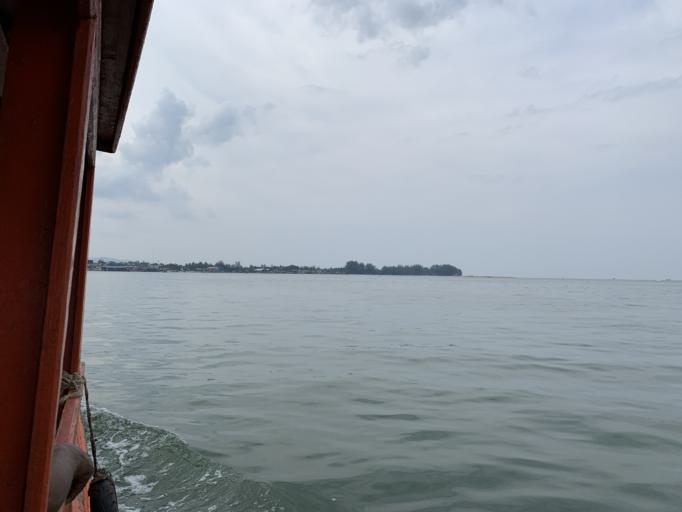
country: TH
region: Phangnga
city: Takua Pa
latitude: 8.8754
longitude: 98.2730
